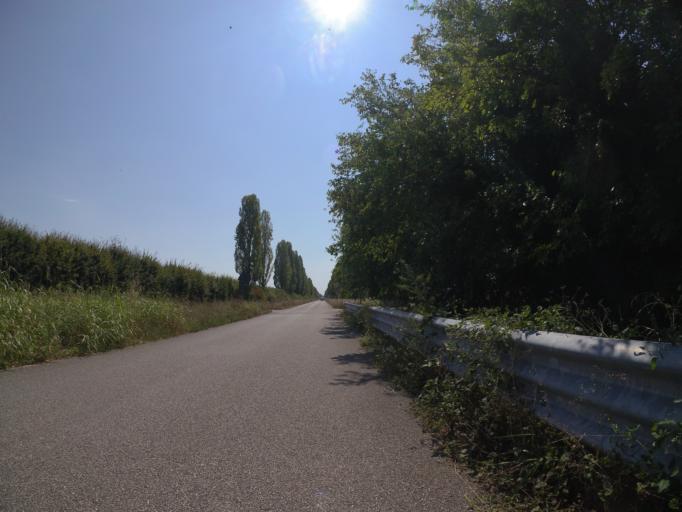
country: IT
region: Friuli Venezia Giulia
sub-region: Provincia di Udine
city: Codroipo
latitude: 45.9672
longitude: 13.0110
